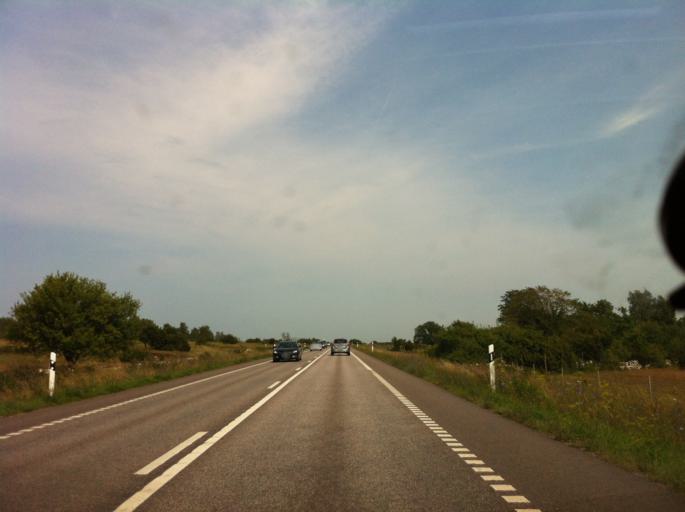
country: SE
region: Kalmar
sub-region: Borgholms Kommun
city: Borgholm
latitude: 56.8400
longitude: 16.6318
